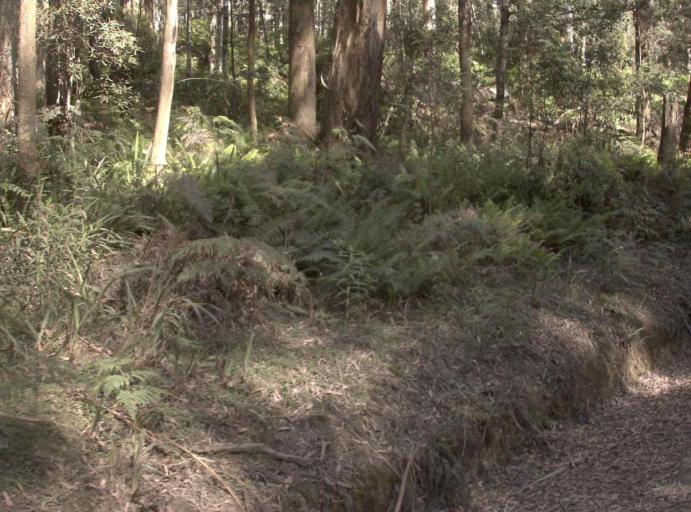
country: AU
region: New South Wales
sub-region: Bombala
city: Bombala
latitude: -37.2331
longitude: 148.7539
